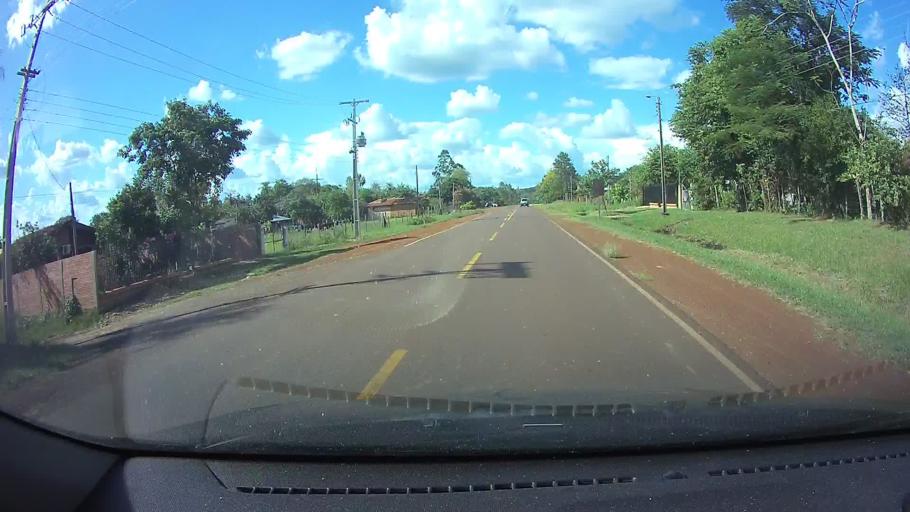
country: PY
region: Cordillera
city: Itacurubi de la Cordillera
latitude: -25.4703
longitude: -56.8802
